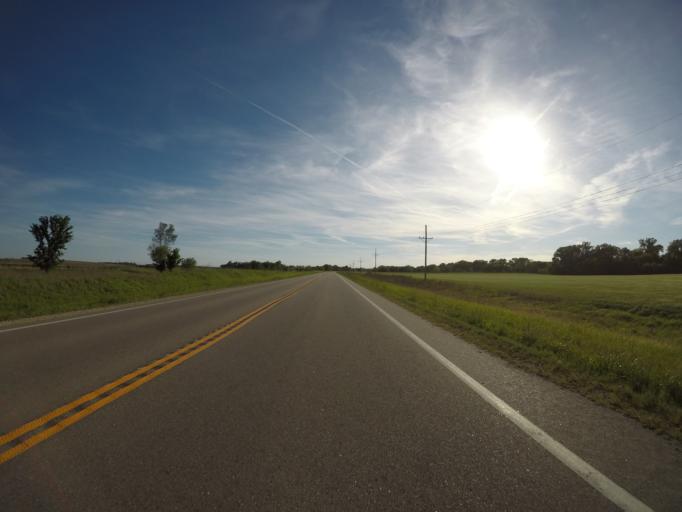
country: US
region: Kansas
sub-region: Cloud County
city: Concordia
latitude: 39.5742
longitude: -97.4263
